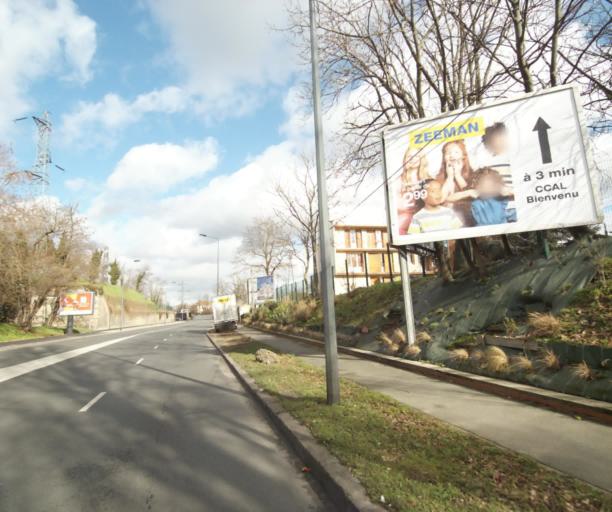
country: FR
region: Ile-de-France
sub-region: Departement de Seine-Saint-Denis
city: Villetaneuse
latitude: 48.9446
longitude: 2.3424
